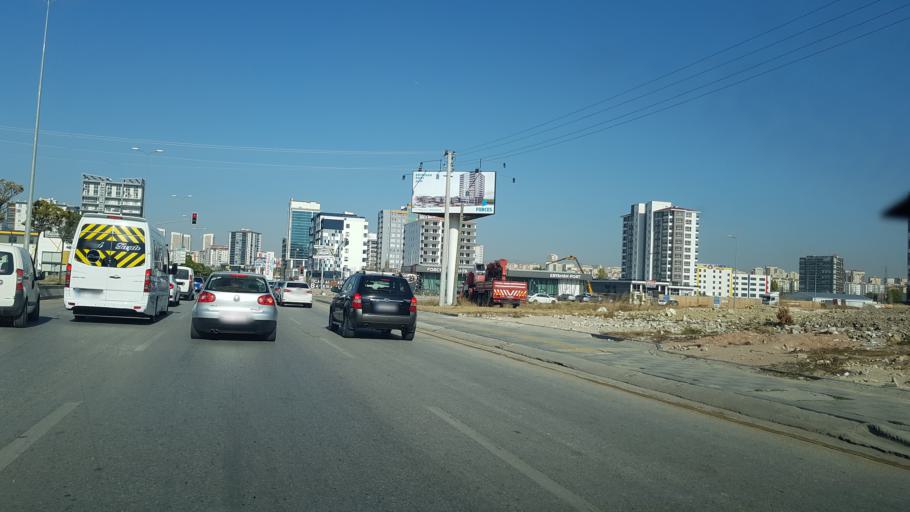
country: TR
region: Ankara
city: Etimesgut
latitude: 39.9635
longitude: 32.6066
